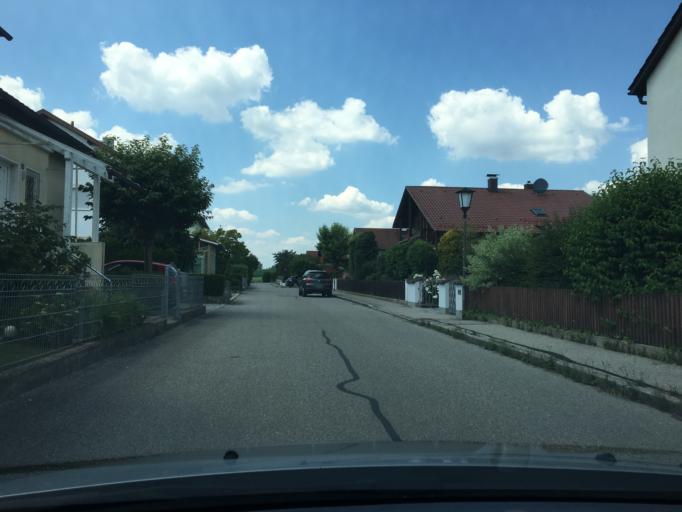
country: DE
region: Bavaria
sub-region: Upper Bavaria
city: Neumarkt-Sankt Veit
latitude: 48.3679
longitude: 12.5064
